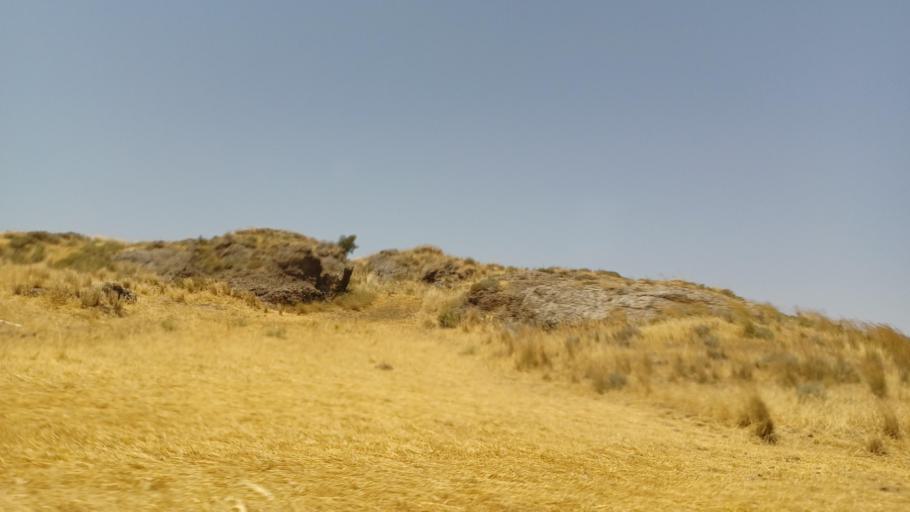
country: CY
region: Larnaka
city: Troulloi
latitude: 35.0221
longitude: 33.6360
